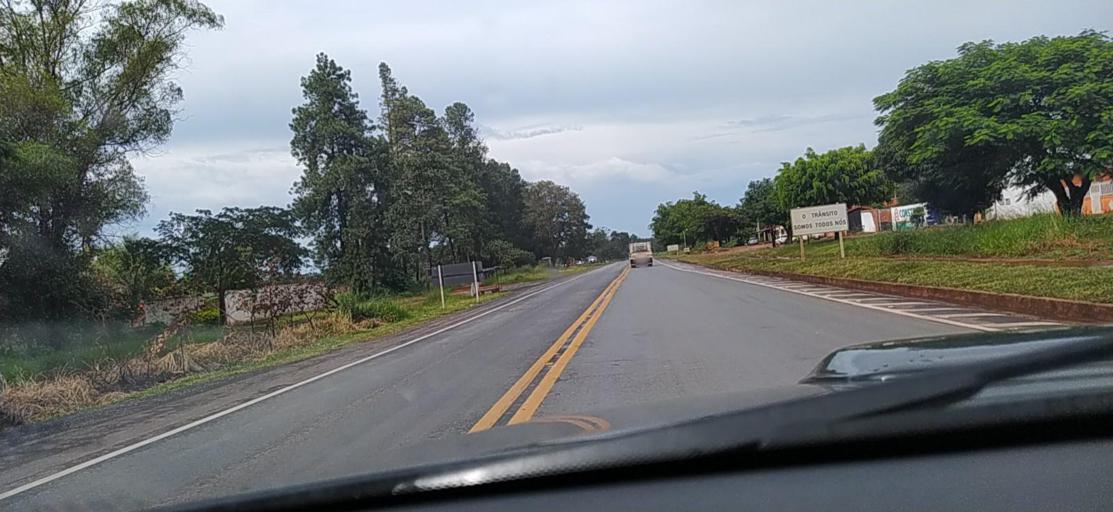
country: BR
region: Minas Gerais
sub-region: Montes Claros
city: Montes Claros
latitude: -16.8782
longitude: -43.8620
